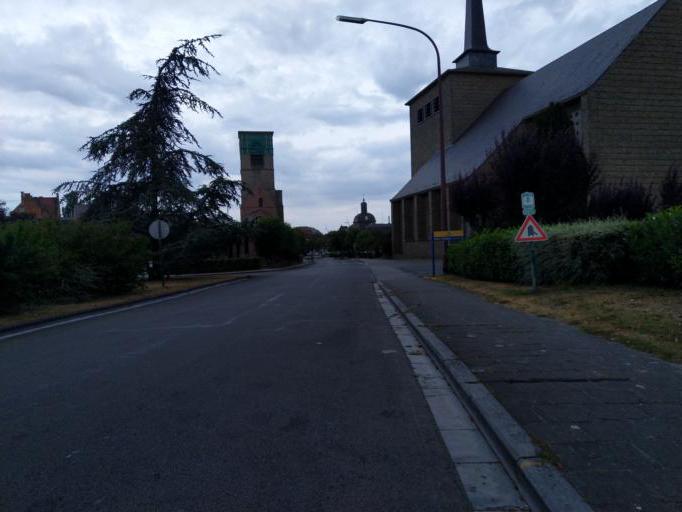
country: BE
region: Wallonia
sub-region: Province du Hainaut
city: Saint-Ghislain
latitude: 50.4475
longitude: 3.8218
